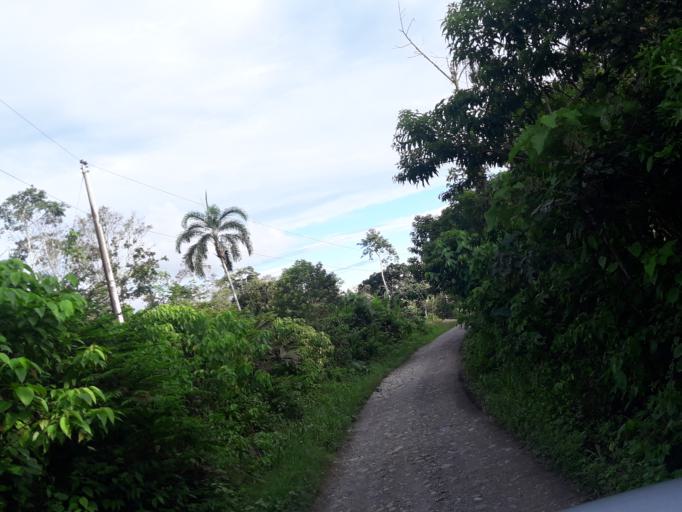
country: EC
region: Orellana
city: Boca Suno
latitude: -0.8983
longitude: -77.3091
